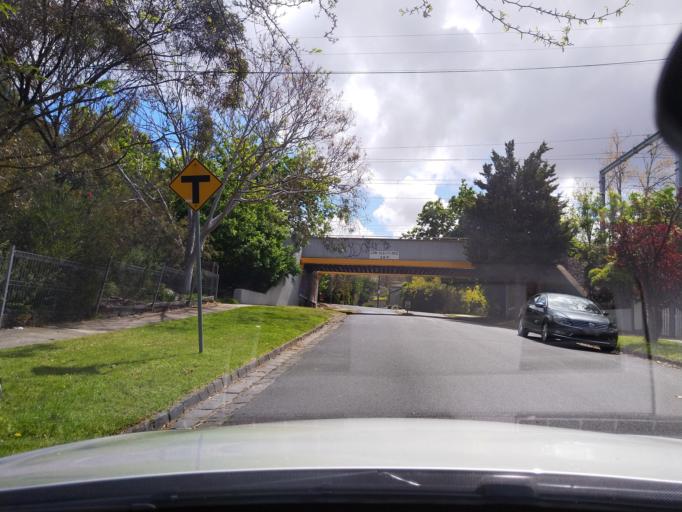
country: AU
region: Victoria
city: Ivanhoe East
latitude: -37.7659
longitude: 145.0515
